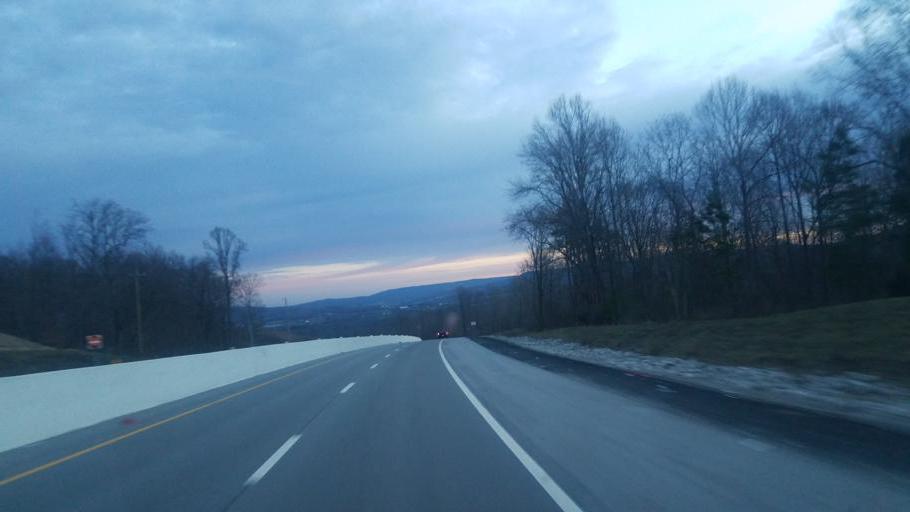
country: US
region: Tennessee
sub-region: Van Buren County
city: Spencer
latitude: 35.7874
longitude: -85.4593
